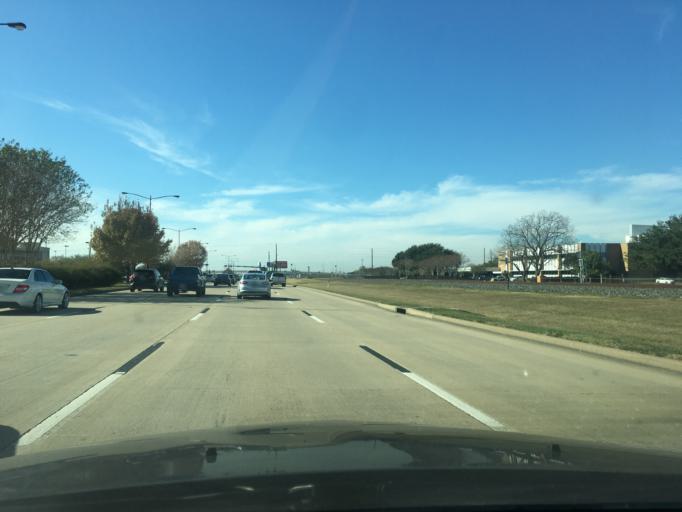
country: US
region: Texas
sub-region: Fort Bend County
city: Sugar Land
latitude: 29.6176
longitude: -95.6414
